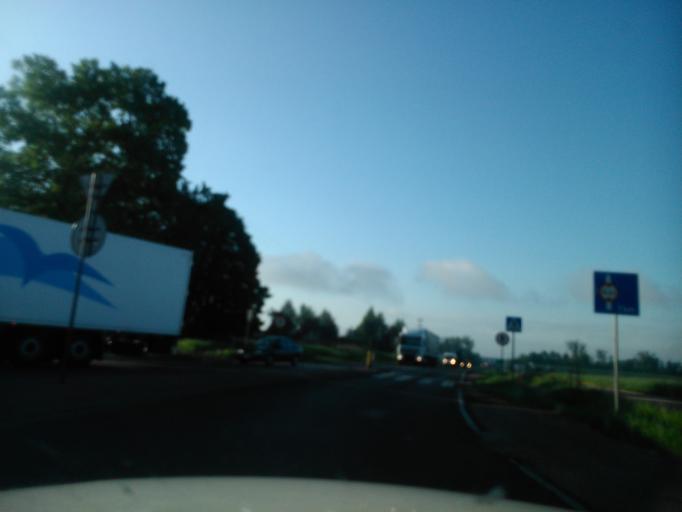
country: PL
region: Masovian Voivodeship
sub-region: Powiat plocki
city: Wyszogrod
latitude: 52.3921
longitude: 20.1796
